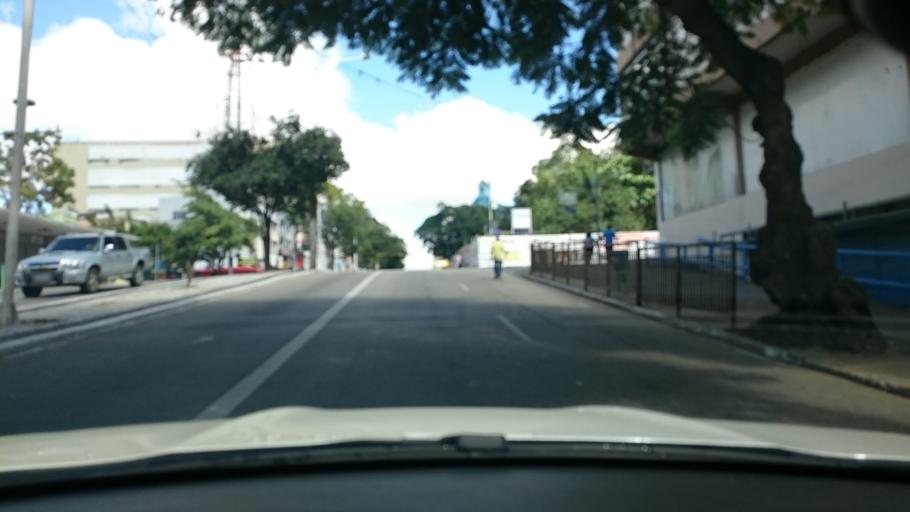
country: BR
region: Paraiba
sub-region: Campina Grande
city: Campina Grande
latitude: -7.2195
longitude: -35.8842
